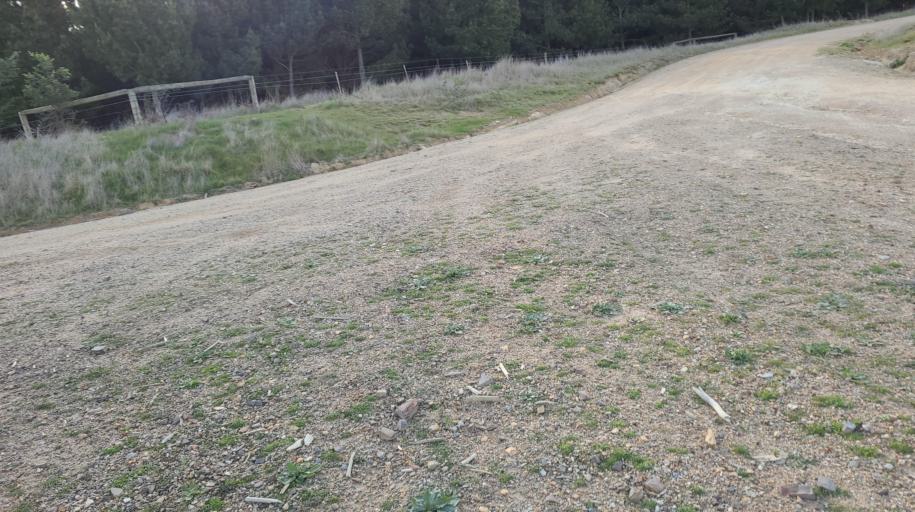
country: AU
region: New South Wales
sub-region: Blayney
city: Millthorpe
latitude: -33.4018
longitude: 149.3159
